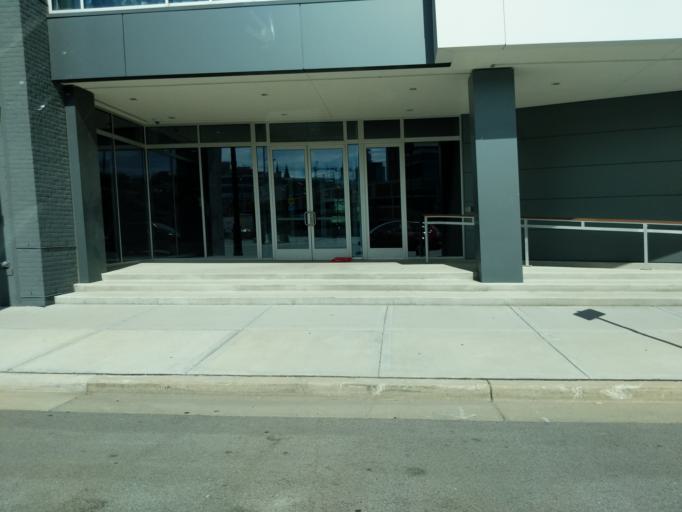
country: US
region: Wisconsin
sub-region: Milwaukee County
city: Milwaukee
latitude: 43.0485
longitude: -87.9101
